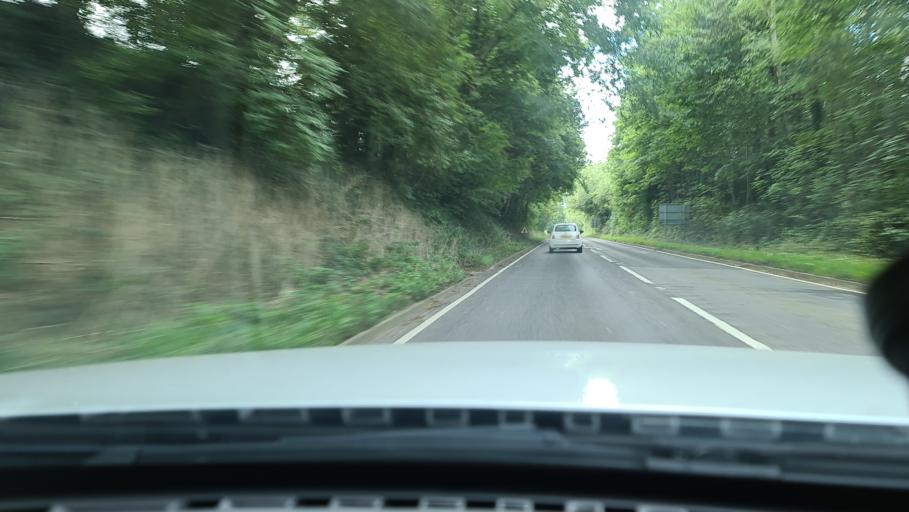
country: GB
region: England
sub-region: Oxfordshire
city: Chipping Norton
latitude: 51.9633
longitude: -1.5322
